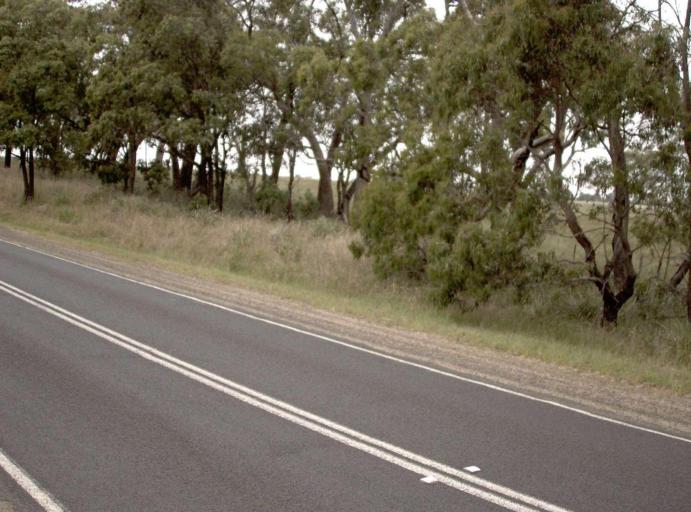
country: AU
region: Victoria
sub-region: Latrobe
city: Traralgon
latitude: -38.2401
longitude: 146.5061
